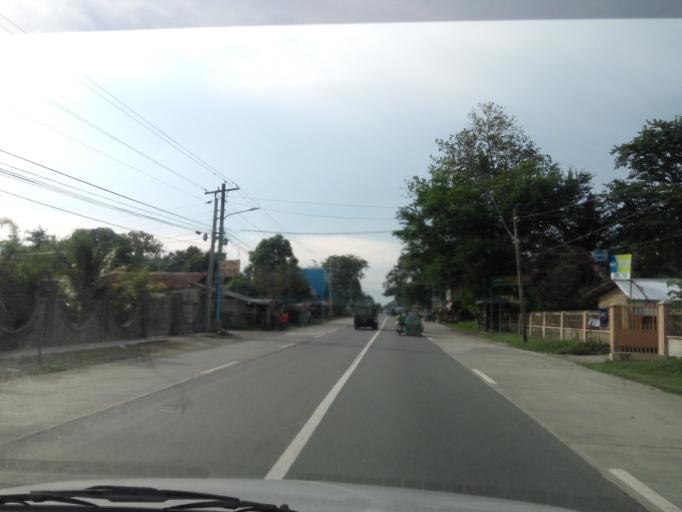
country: PH
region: Ilocos
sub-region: Province of Pangasinan
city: Binalonan
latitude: 16.0805
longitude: 120.5826
